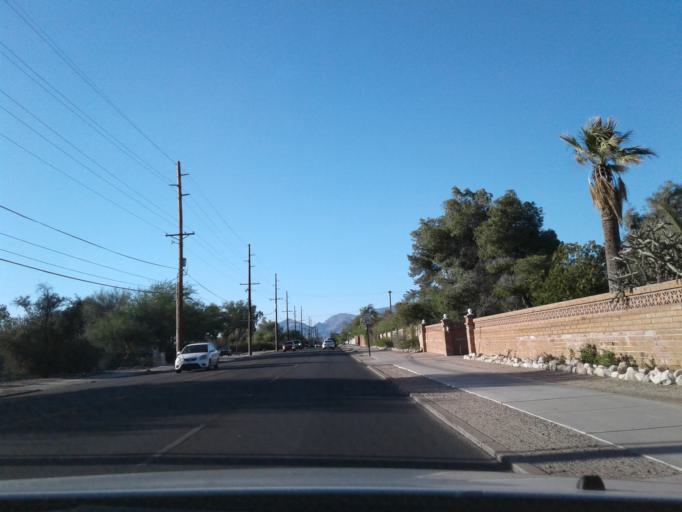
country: US
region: Arizona
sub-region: Pima County
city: Tucson
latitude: 32.2168
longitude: -110.9265
